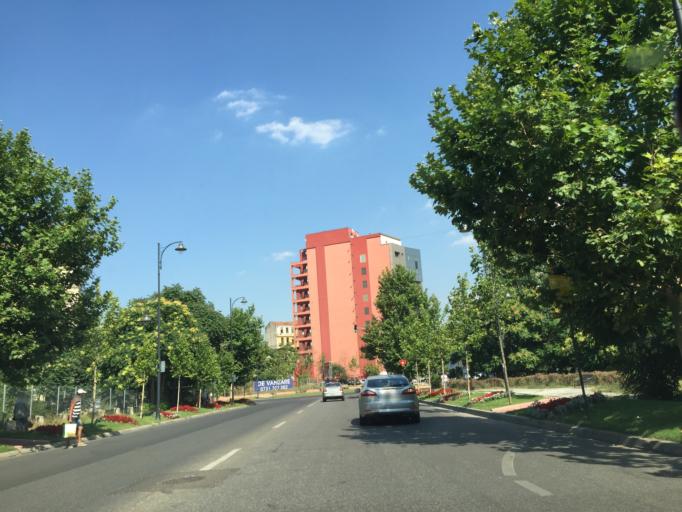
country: RO
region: Bucuresti
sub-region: Municipiul Bucuresti
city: Bucharest
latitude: 44.4282
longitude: 26.1108
